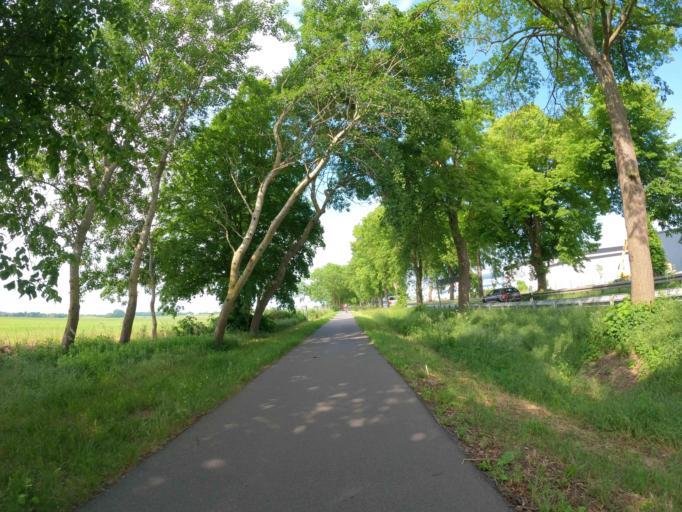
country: DE
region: Mecklenburg-Vorpommern
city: Wendorf
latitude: 54.2816
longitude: 13.0462
